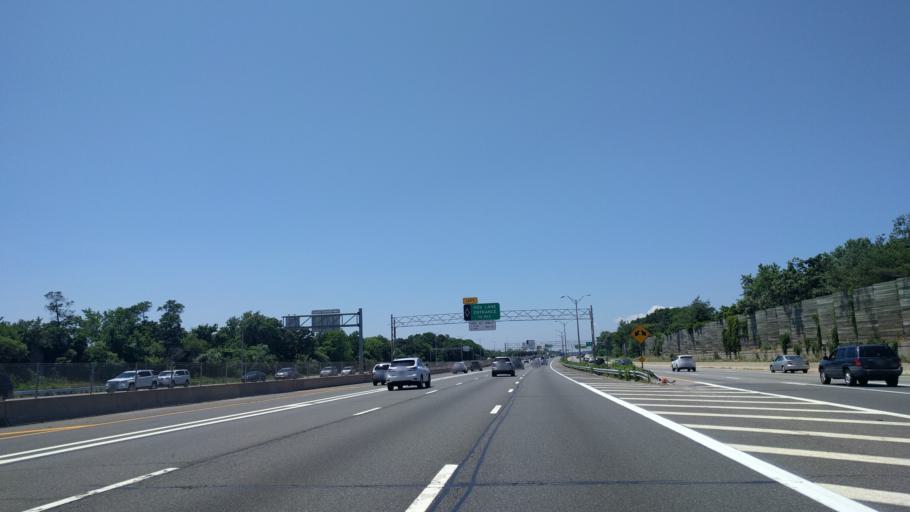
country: US
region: New York
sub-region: Suffolk County
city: Brentwood
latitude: 40.8051
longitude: -73.2570
